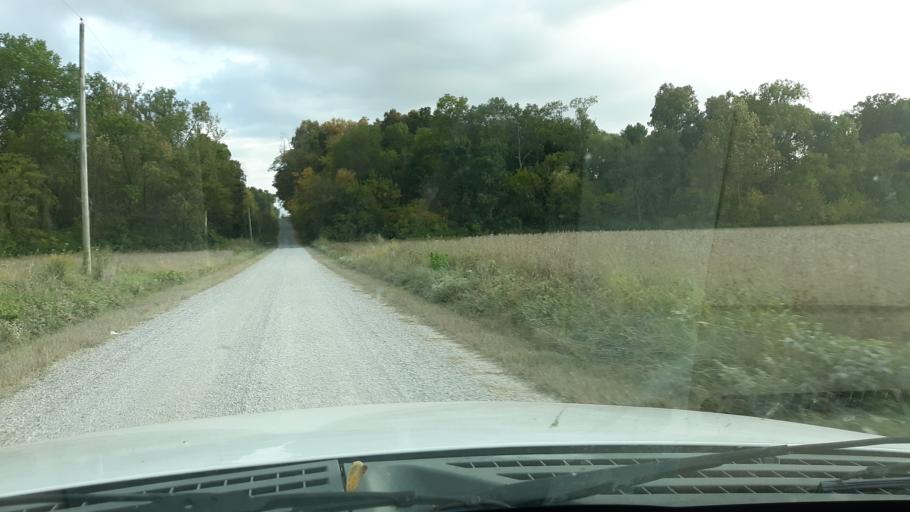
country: US
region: Illinois
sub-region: Saline County
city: Eldorado
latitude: 37.8320
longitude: -88.5026
